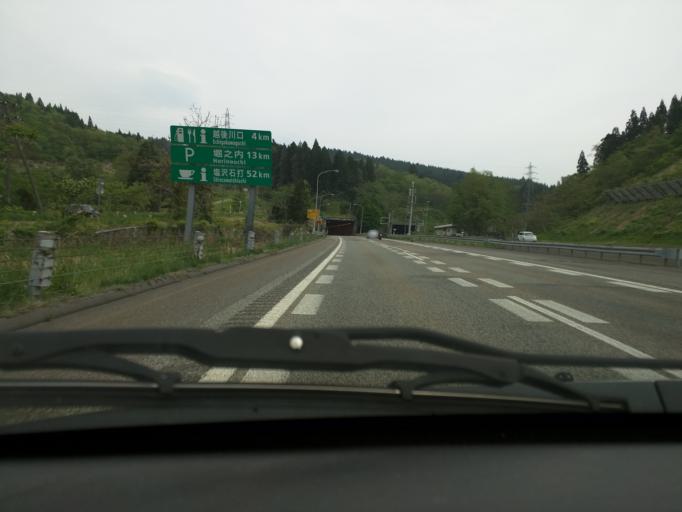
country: JP
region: Niigata
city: Ojiya
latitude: 37.2782
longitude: 138.7903
